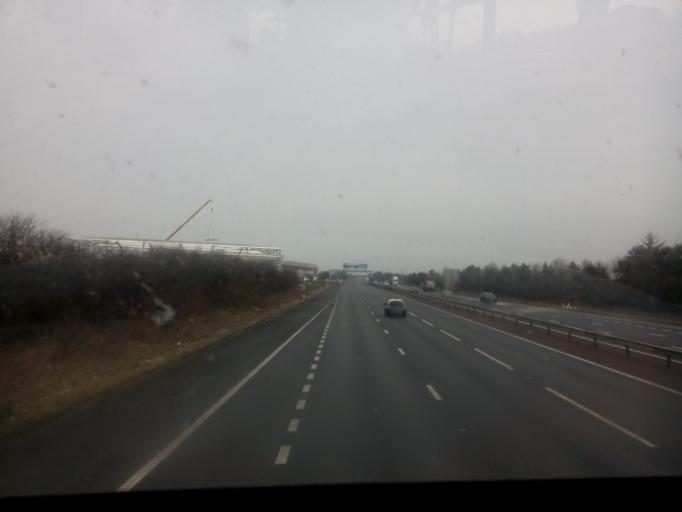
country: GB
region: England
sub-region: County Durham
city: Chester-le-Street
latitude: 54.8928
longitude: -1.5593
